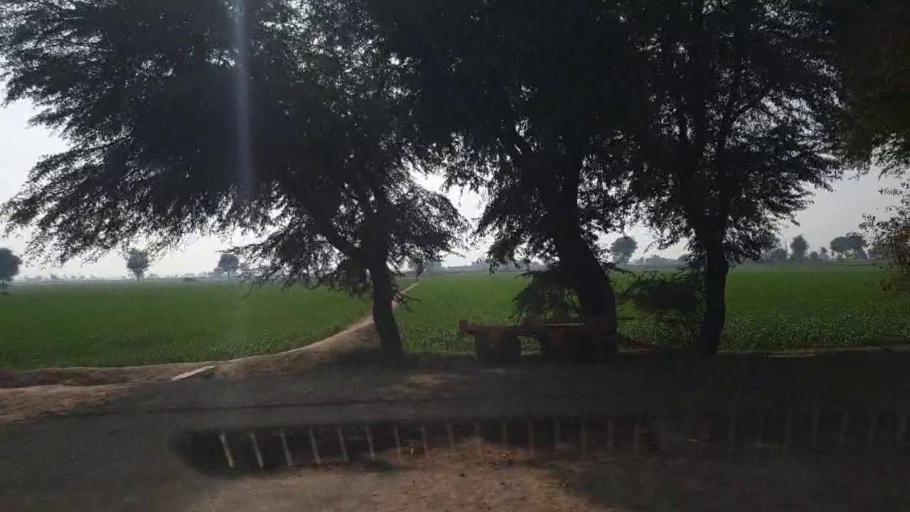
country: PK
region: Sindh
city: Shahdadpur
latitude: 26.0195
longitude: 68.5744
